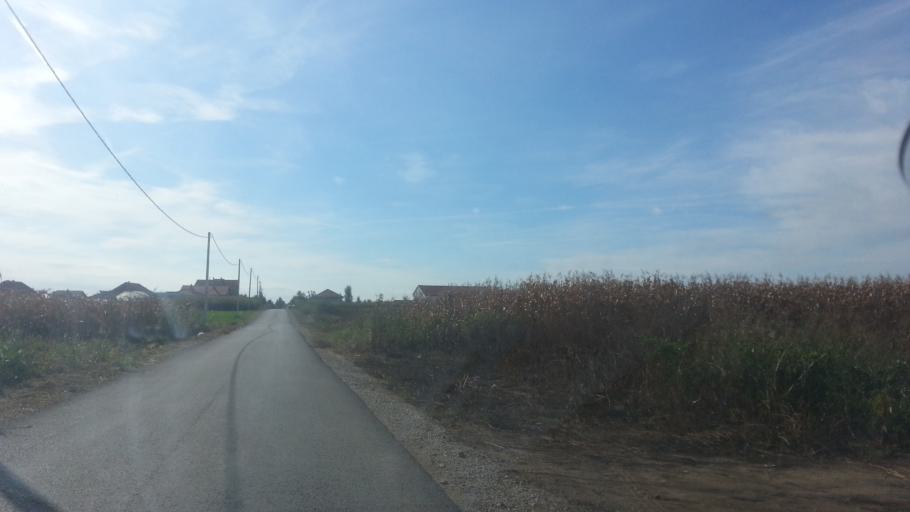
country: RS
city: Stari Banovci
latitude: 44.9754
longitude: 20.2720
